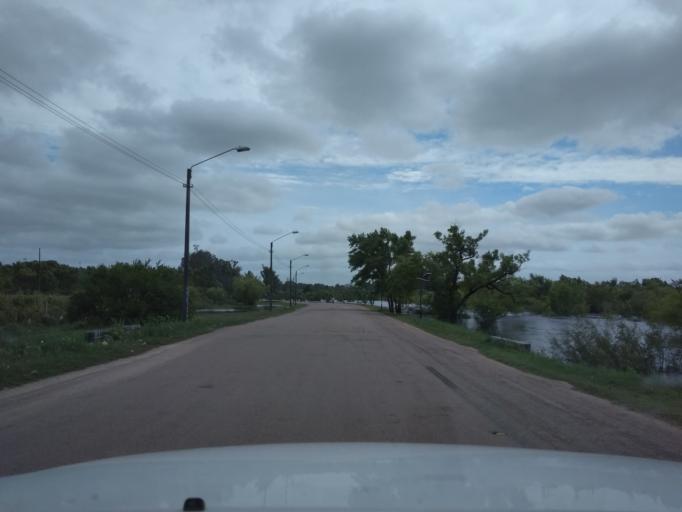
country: UY
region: Florida
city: Florida
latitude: -34.1055
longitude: -56.2045
